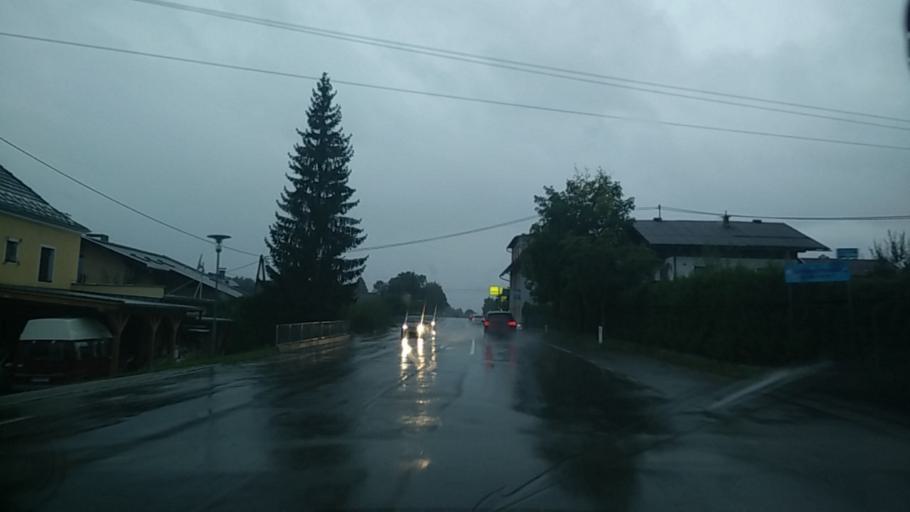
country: AT
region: Carinthia
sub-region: Politischer Bezirk Villach Land
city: Wernberg
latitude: 46.6173
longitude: 13.9581
